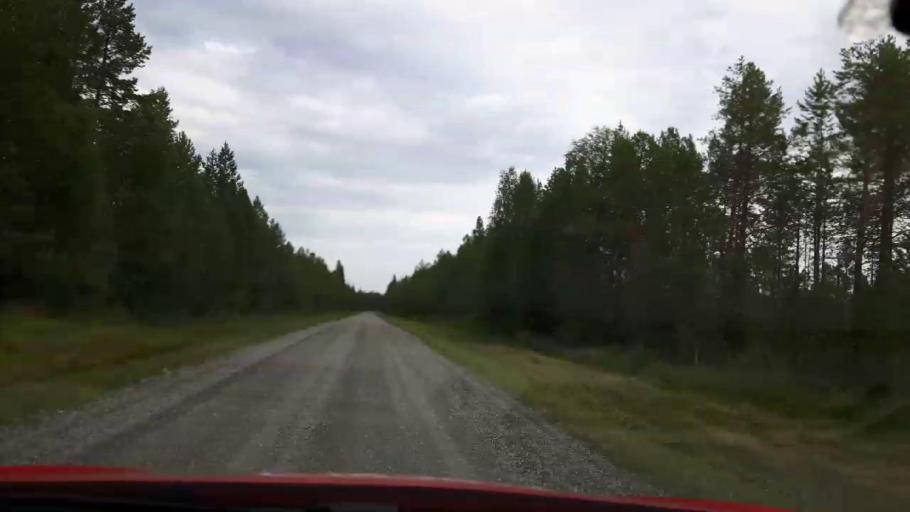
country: SE
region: Jaemtland
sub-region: Stroemsunds Kommun
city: Stroemsund
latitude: 63.7342
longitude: 15.5555
